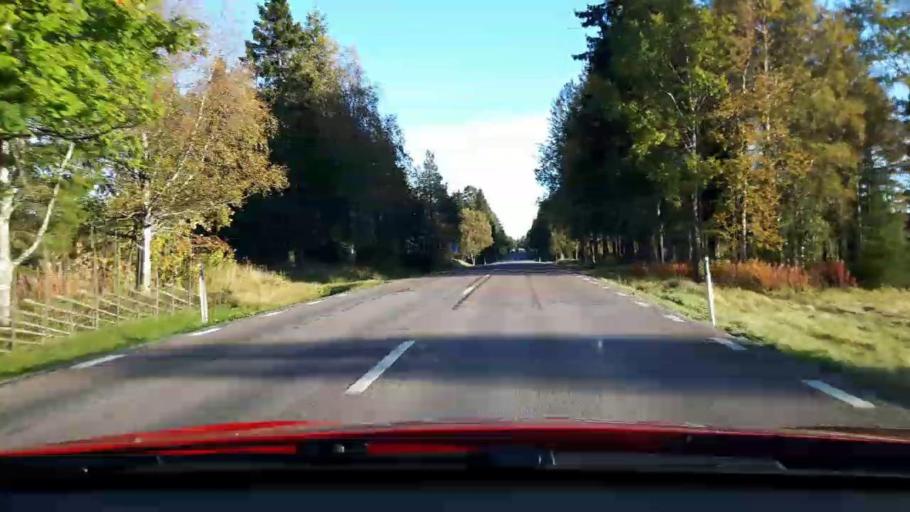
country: SE
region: Jaemtland
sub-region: OEstersunds Kommun
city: Brunflo
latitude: 63.0563
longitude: 14.8564
